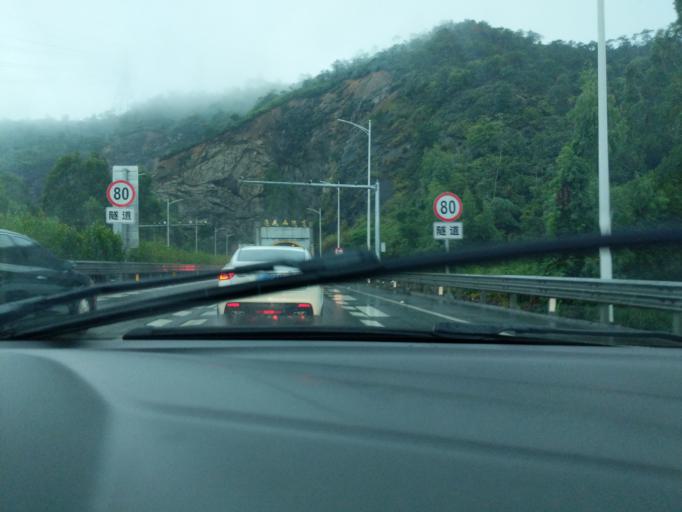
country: CN
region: Guangdong
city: Canghou
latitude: 22.5823
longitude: 113.0344
